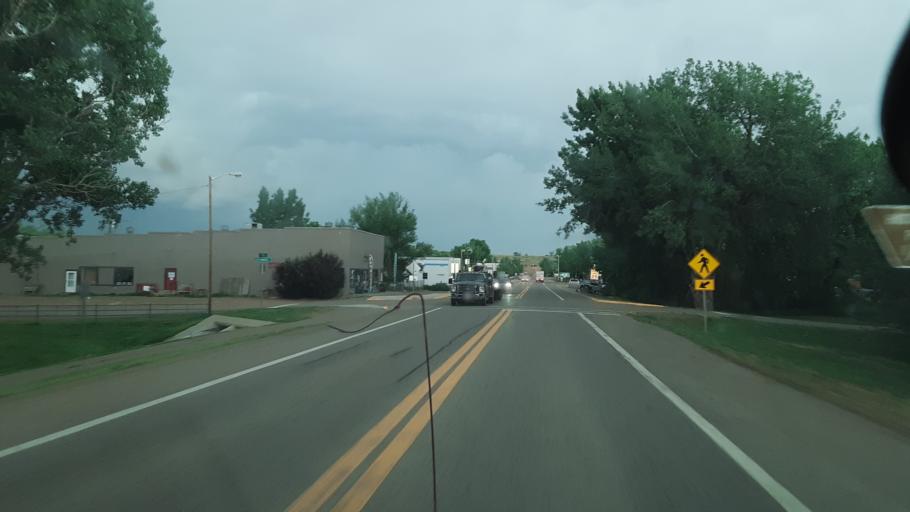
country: US
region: Montana
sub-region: Powder River County
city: Broadus
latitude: 45.4405
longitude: -105.4083
